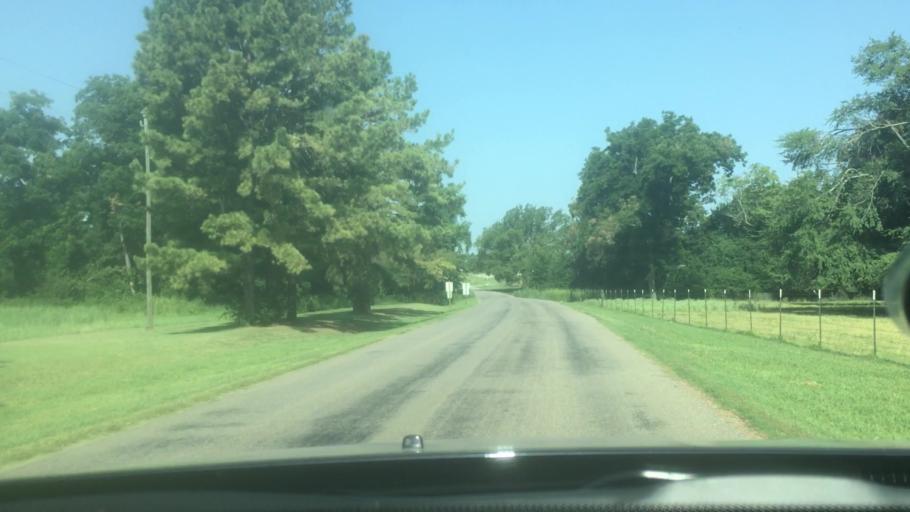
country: US
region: Oklahoma
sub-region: Bryan County
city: Calera
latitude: 33.9399
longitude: -96.4483
